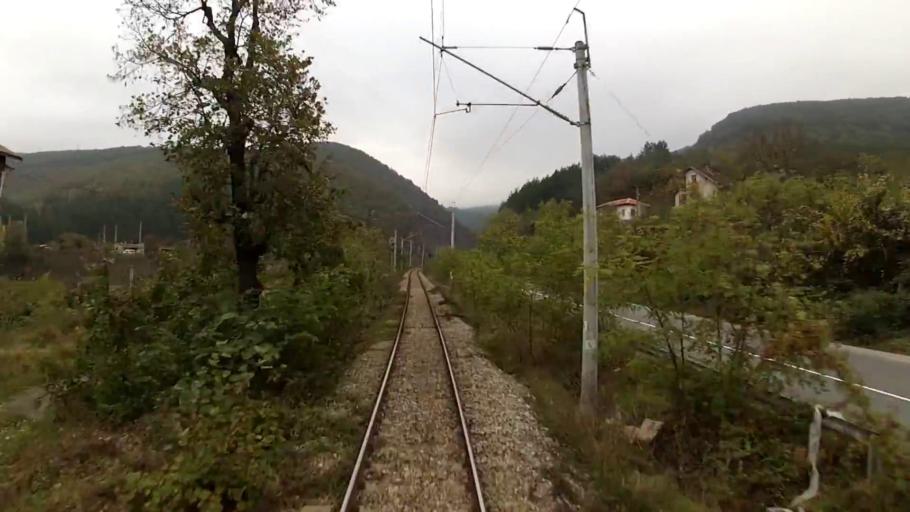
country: RS
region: Central Serbia
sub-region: Pirotski Okrug
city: Dimitrovgrad
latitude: 42.9775
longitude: 22.8495
